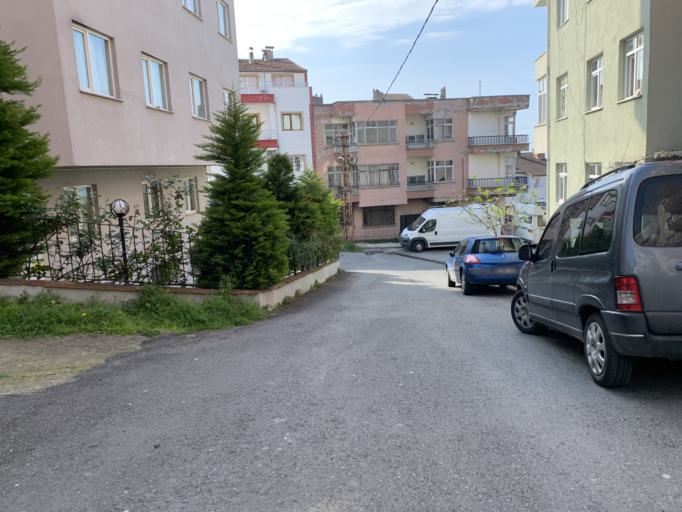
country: TR
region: Trabzon
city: Trabzon
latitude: 40.9963
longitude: 39.7605
